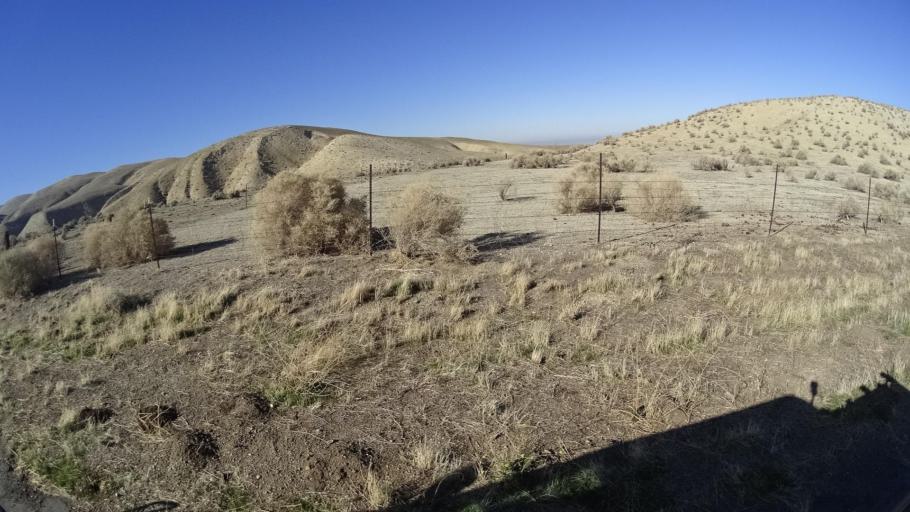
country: US
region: California
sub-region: Kern County
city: Maricopa
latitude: 34.9841
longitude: -119.3954
